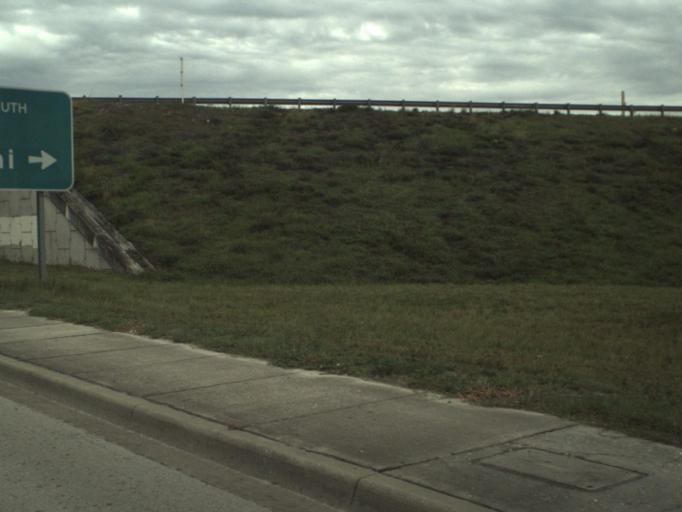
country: US
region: Florida
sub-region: Palm Beach County
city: Lake Belvedere Estates
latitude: 26.6795
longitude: -80.1654
